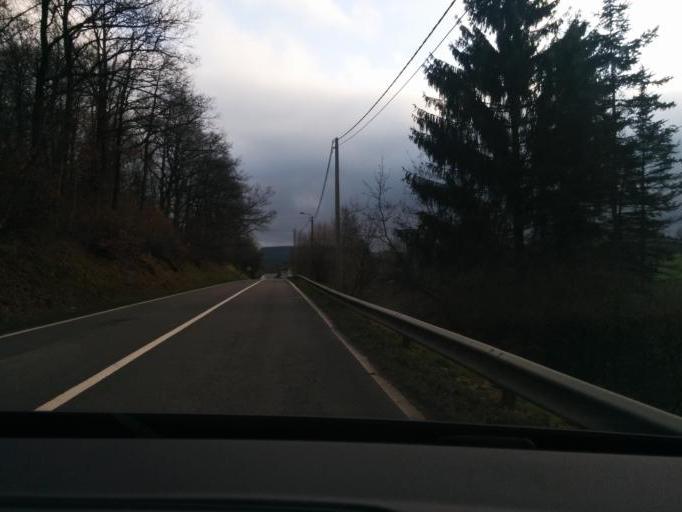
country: BE
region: Wallonia
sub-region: Province du Luxembourg
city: Gouvy
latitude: 50.1882
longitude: 5.9364
